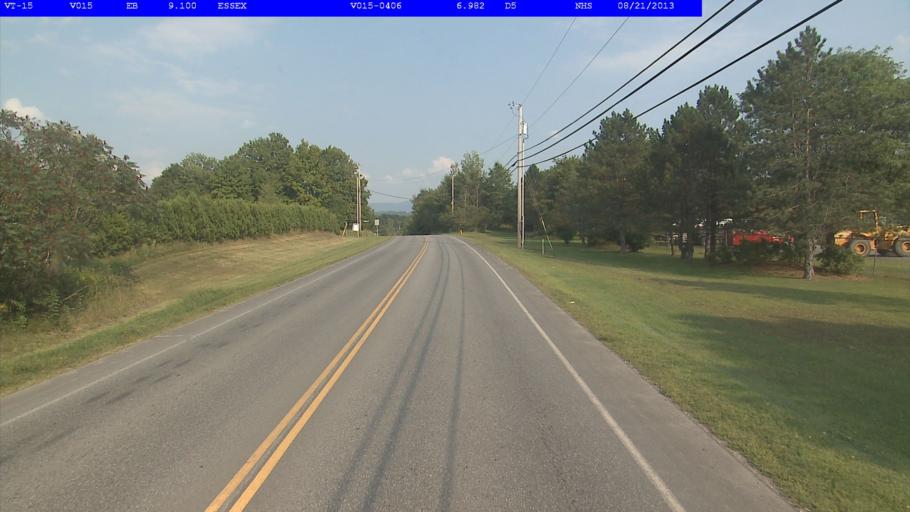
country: US
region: Vermont
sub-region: Chittenden County
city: Jericho
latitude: 44.5023
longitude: -73.0300
